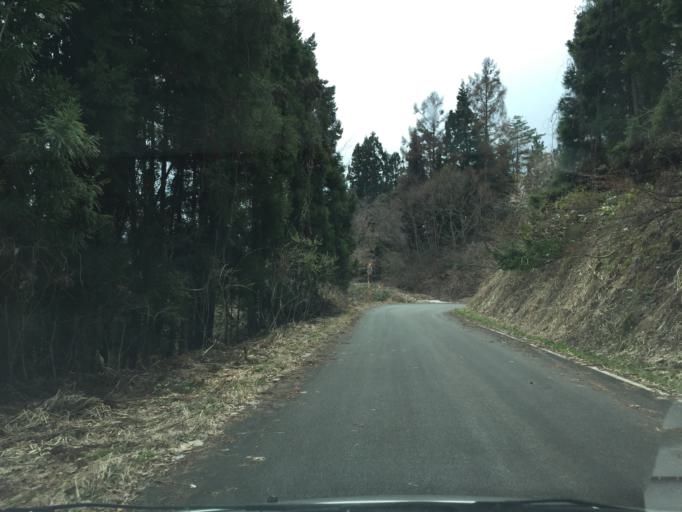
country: JP
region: Fukushima
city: Kitakata
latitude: 37.4756
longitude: 139.8094
